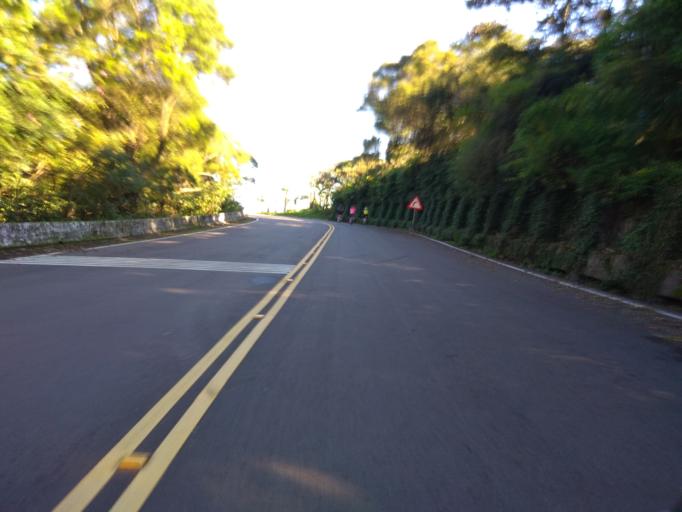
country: TW
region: Taiwan
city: Daxi
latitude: 24.8931
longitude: 121.1488
